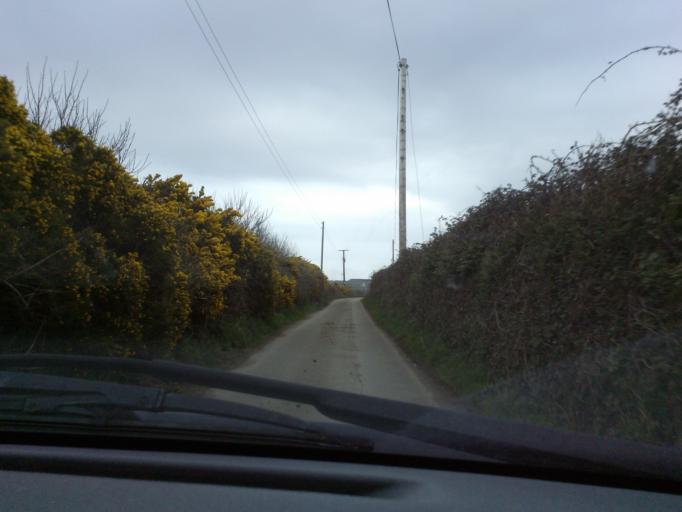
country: GB
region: England
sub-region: Cornwall
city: Saint Just
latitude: 50.1058
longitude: -5.6638
